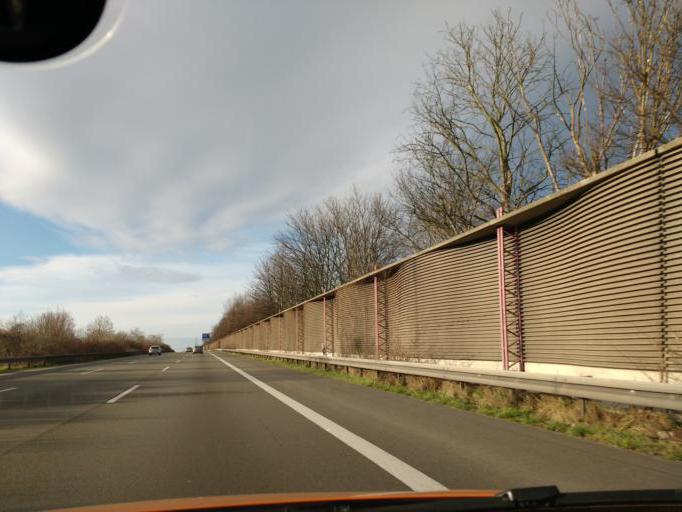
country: DE
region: Lower Saxony
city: Wendeburg
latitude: 52.3388
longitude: 10.3841
